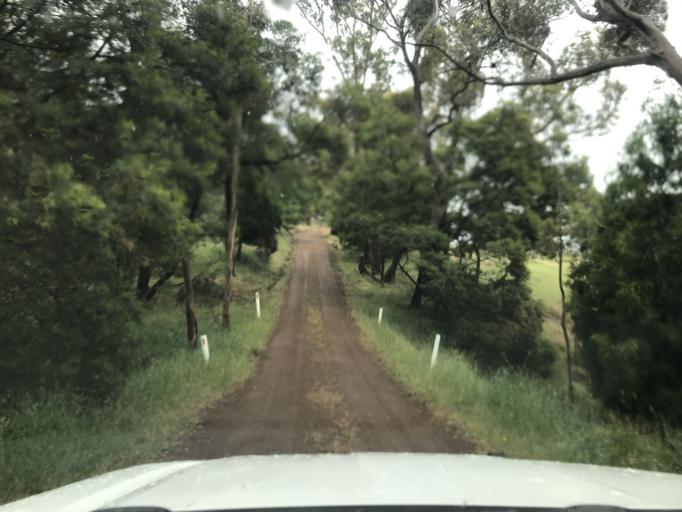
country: AU
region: South Australia
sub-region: Wattle Range
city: Penola
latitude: -37.2635
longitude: 141.3180
